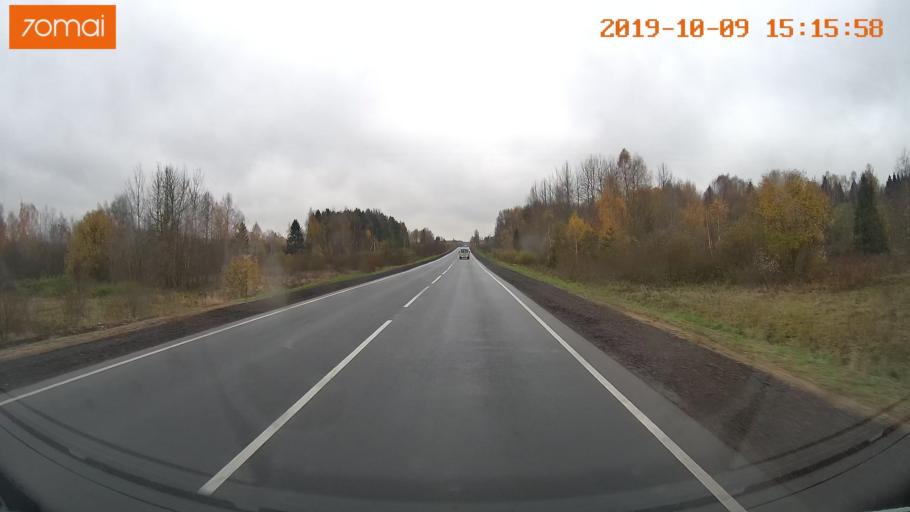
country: RU
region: Kostroma
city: Susanino
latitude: 58.1158
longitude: 41.5876
